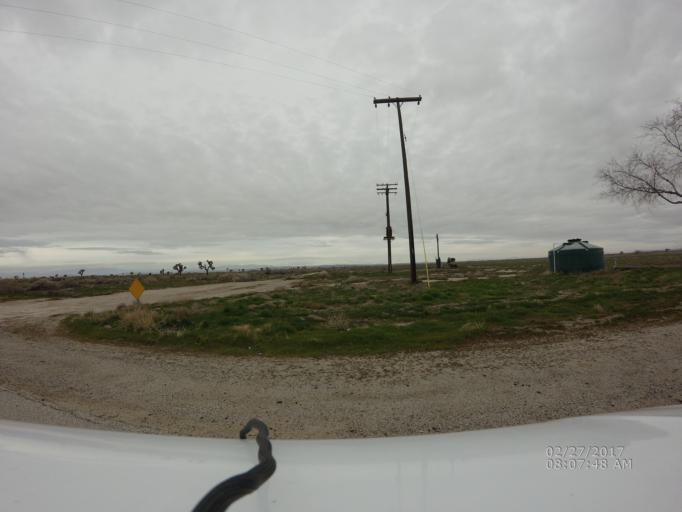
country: US
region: California
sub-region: Los Angeles County
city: Lancaster
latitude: 34.7195
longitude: -117.9874
